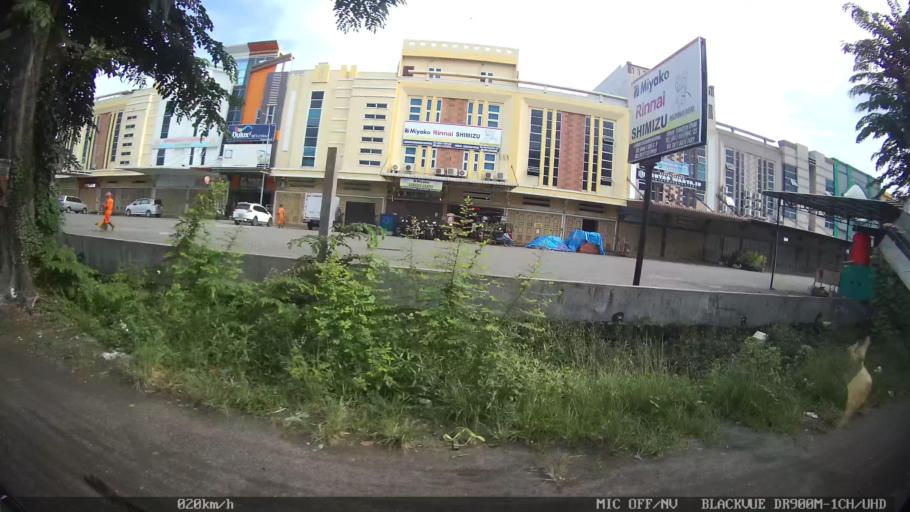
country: ID
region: North Sumatra
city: Medan
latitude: 3.6288
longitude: 98.7029
